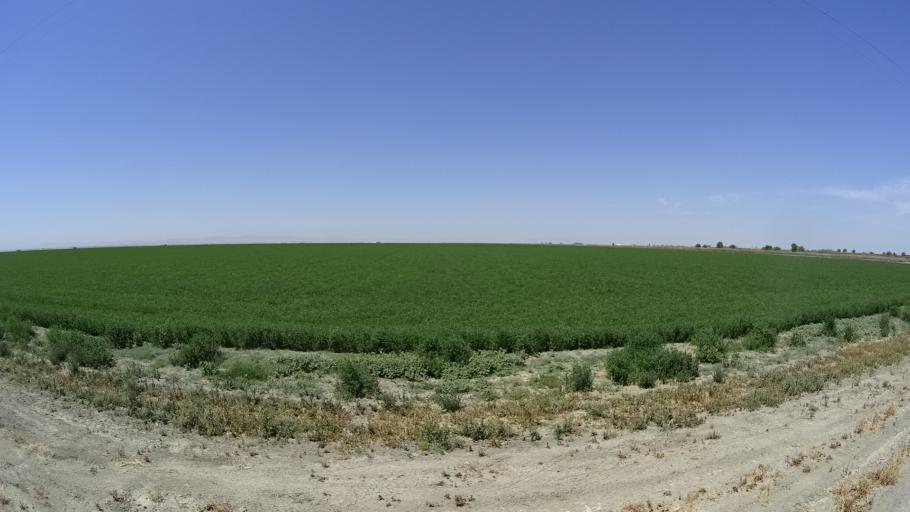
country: US
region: California
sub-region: Kings County
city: Stratford
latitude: 36.1363
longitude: -119.7340
